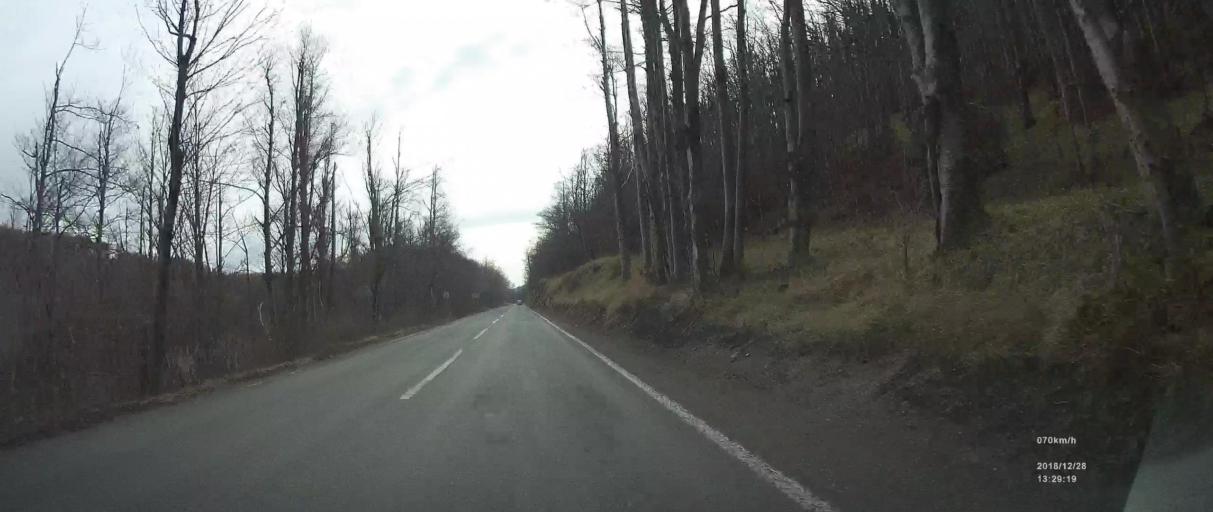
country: HR
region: Primorsko-Goranska
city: Hreljin
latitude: 45.3621
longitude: 14.6274
